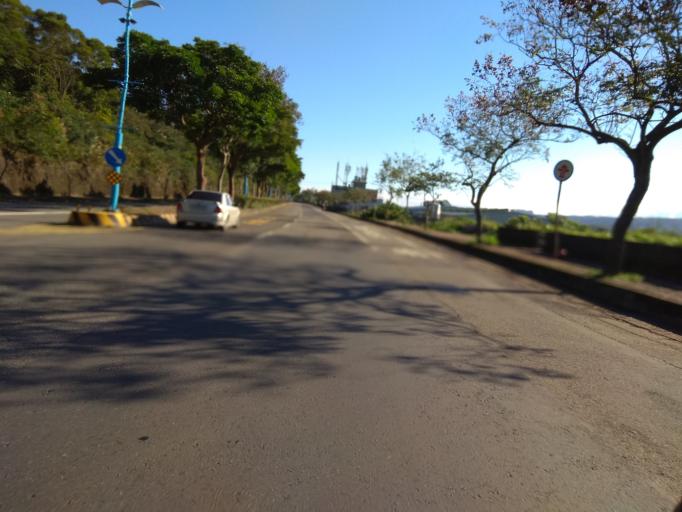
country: TW
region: Taiwan
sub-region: Hsinchu
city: Zhubei
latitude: 24.8972
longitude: 121.1144
